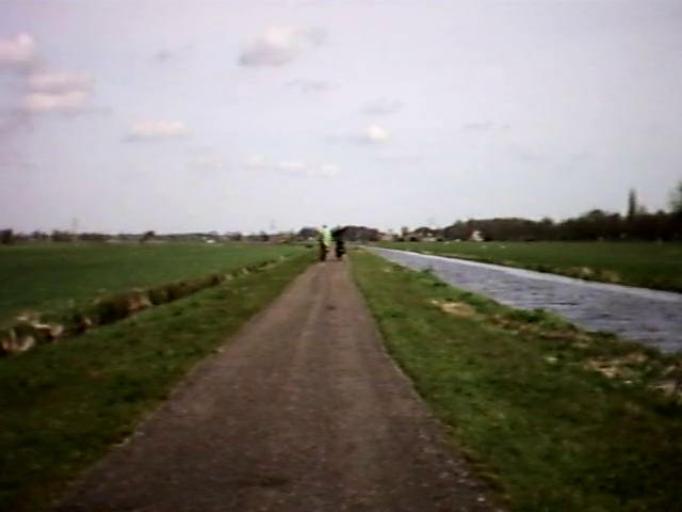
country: NL
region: Utrecht
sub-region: Gemeente De Bilt
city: De Bilt
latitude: 52.1305
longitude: 5.1458
